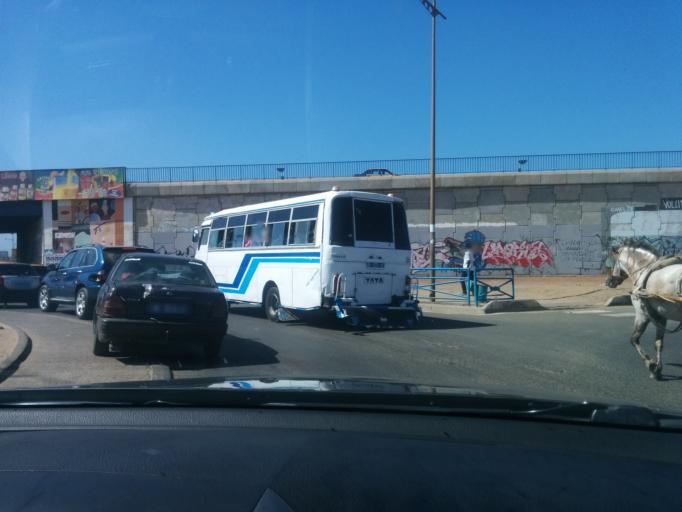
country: SN
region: Dakar
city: Mermoz Boabab
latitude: 14.7156
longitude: -17.4712
